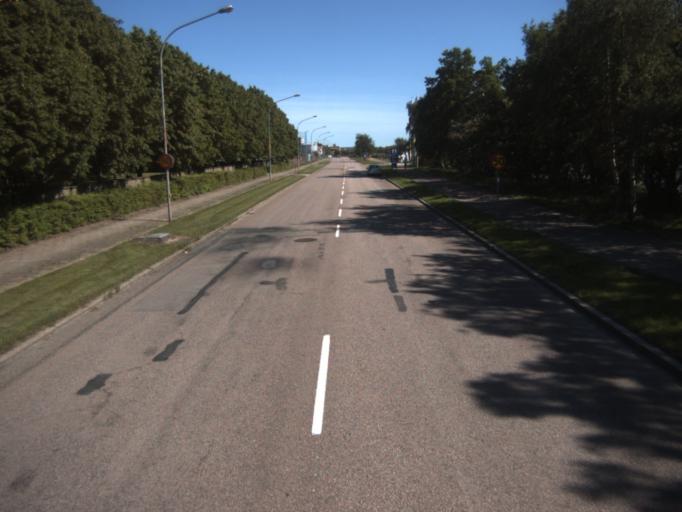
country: SE
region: Skane
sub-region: Helsingborg
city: Rydeback
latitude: 56.0043
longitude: 12.7292
